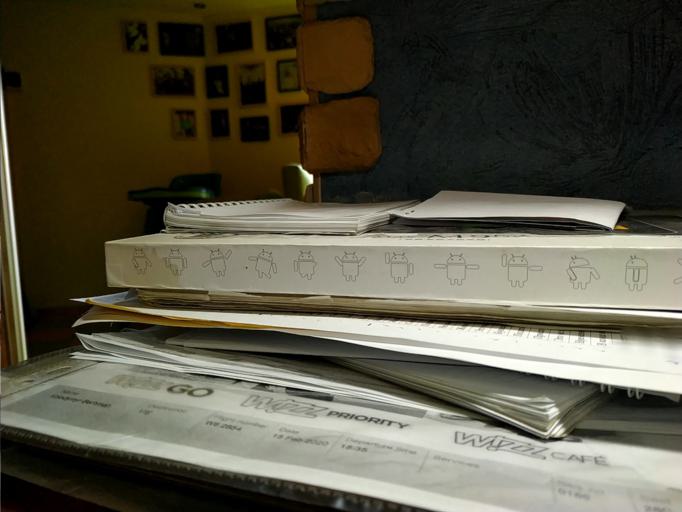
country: RU
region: Pskov
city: Plyussa
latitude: 58.3686
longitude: 29.7370
